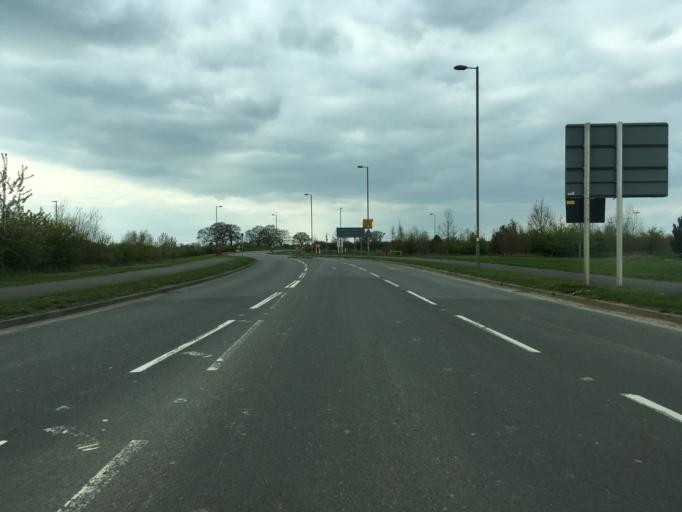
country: GB
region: England
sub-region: Oxfordshire
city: Bicester
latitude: 51.8867
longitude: -1.1705
